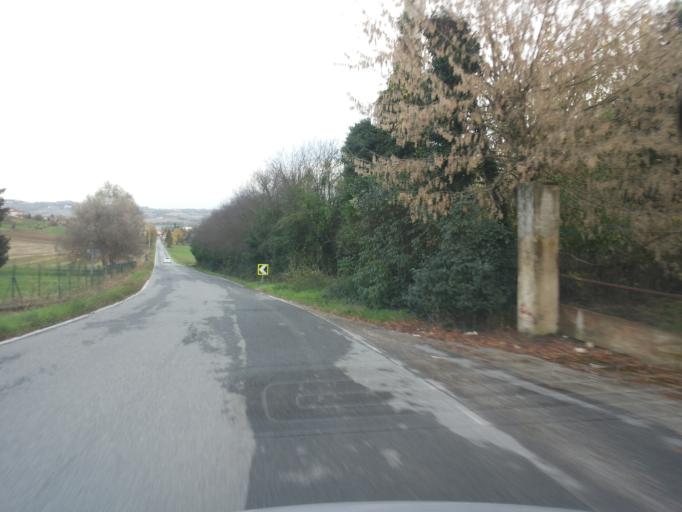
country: IT
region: Piedmont
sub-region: Provincia di Alessandria
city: Serralunga di Crea
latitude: 45.0990
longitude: 8.2934
